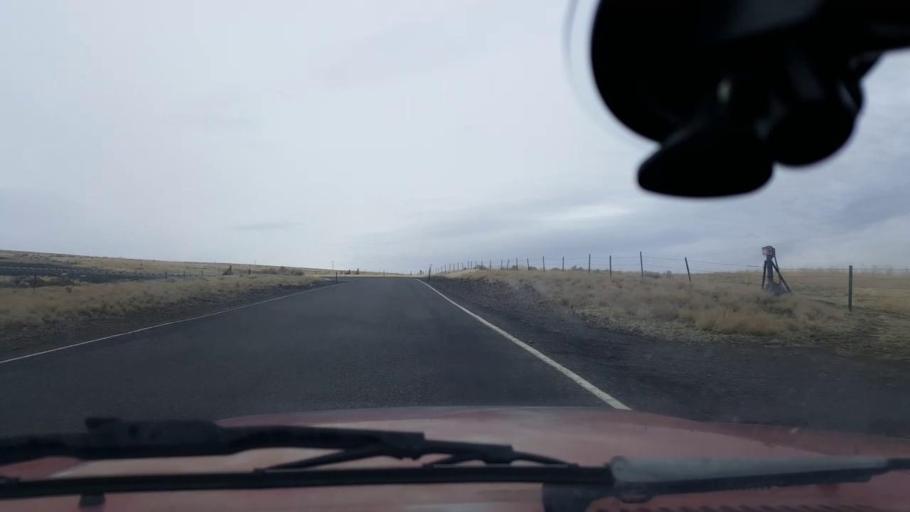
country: US
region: Washington
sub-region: Asotin County
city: Clarkston Heights-Vineland
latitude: 46.3203
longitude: -117.3456
